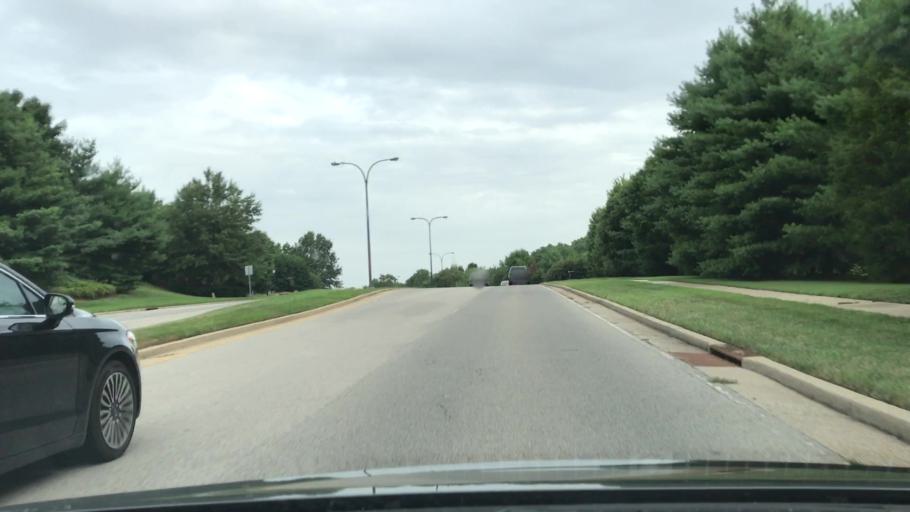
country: US
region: Tennessee
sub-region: Williamson County
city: Franklin
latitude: 35.9380
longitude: -86.7964
